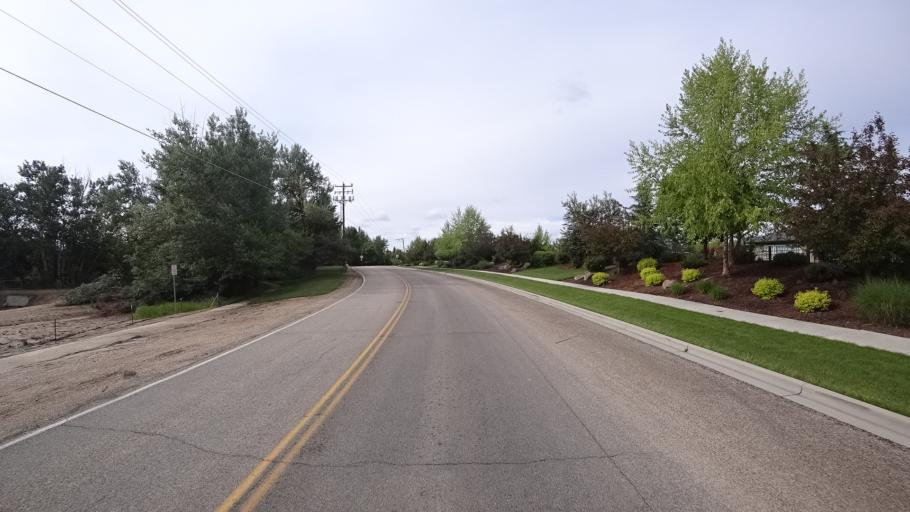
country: US
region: Idaho
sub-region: Ada County
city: Eagle
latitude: 43.7056
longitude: -116.3792
